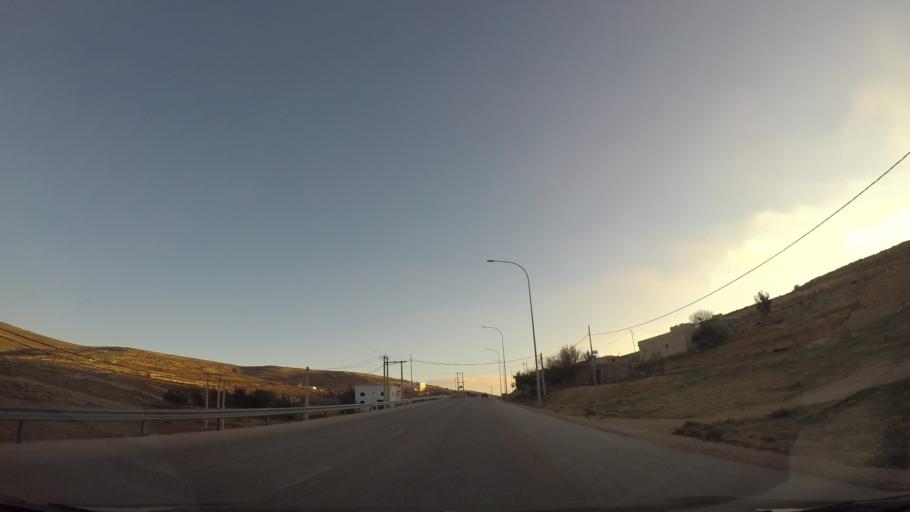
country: JO
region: Ma'an
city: Petra
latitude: 30.4231
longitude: 35.5127
